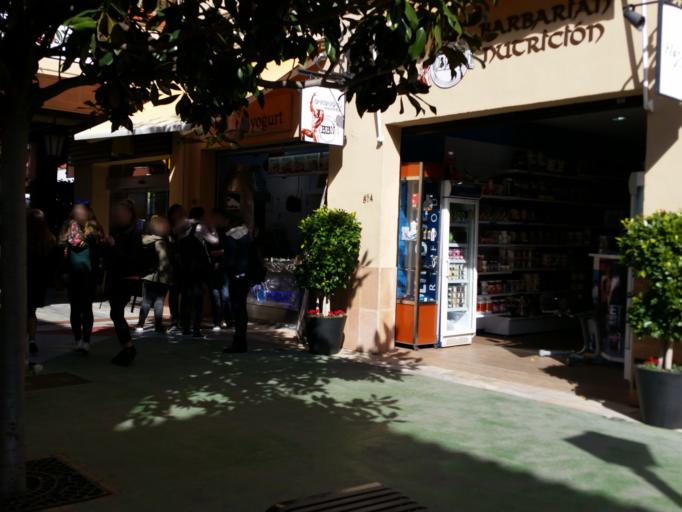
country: ES
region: Andalusia
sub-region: Provincia de Malaga
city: Torremolinos
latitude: 36.6565
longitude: -4.4789
